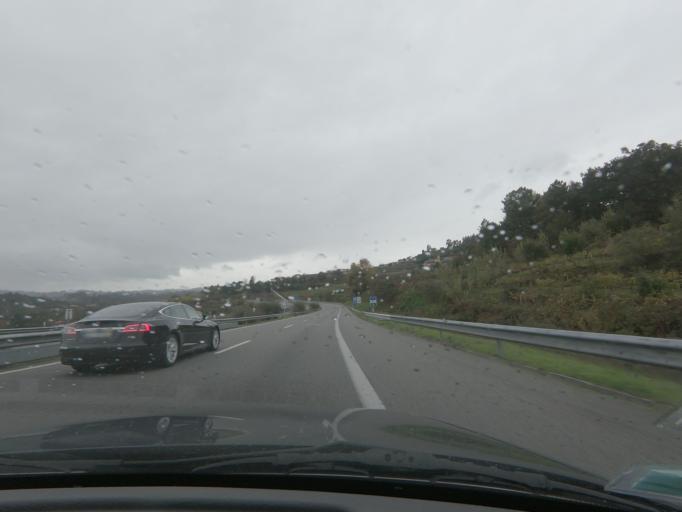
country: PT
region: Porto
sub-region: Marco de Canaveses
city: Marco de Canavezes
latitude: 41.2200
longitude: -8.1567
